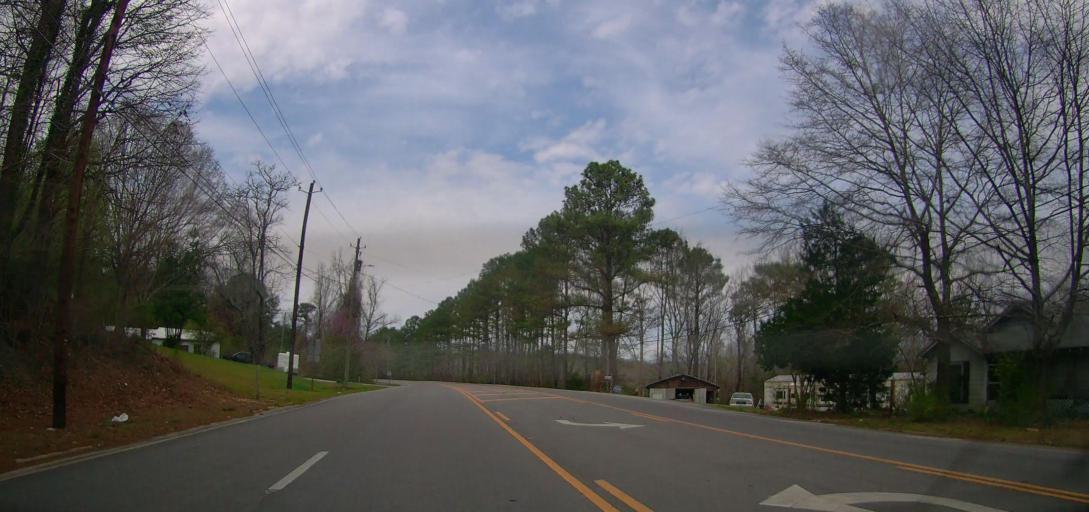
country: US
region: Alabama
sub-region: Marion County
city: Guin
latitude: 33.9813
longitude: -87.9177
